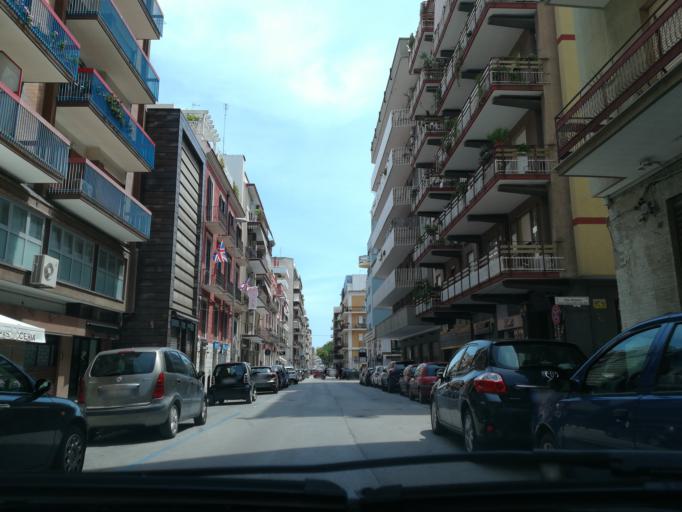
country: IT
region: Apulia
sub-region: Provincia di Barletta - Andria - Trani
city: Barletta
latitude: 41.3180
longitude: 16.2830
